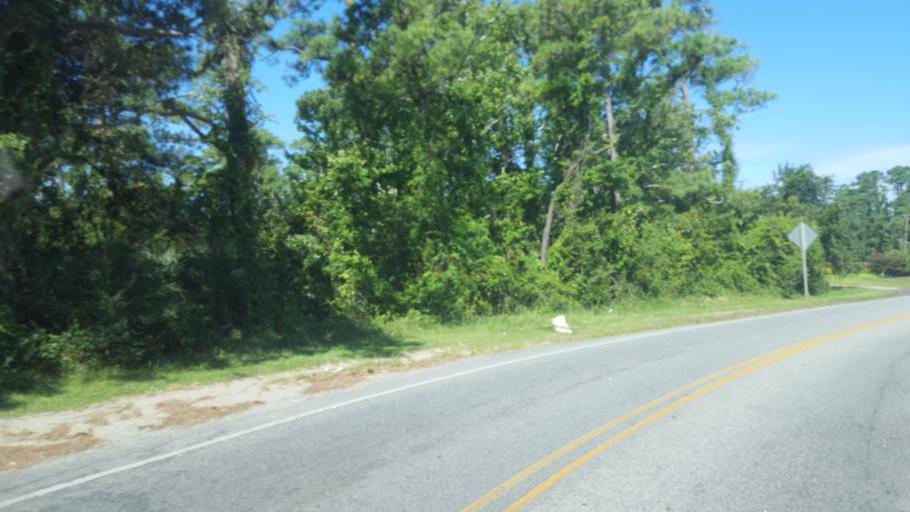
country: US
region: North Carolina
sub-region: Dare County
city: Kill Devil Hills
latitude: 36.0150
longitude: -75.6907
